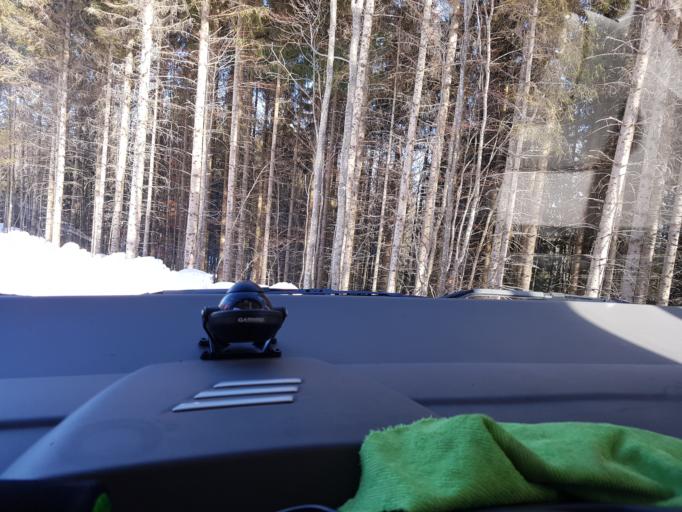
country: FR
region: Alsace
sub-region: Departement du Haut-Rhin
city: Metzeral
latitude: 47.9866
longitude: 7.0479
